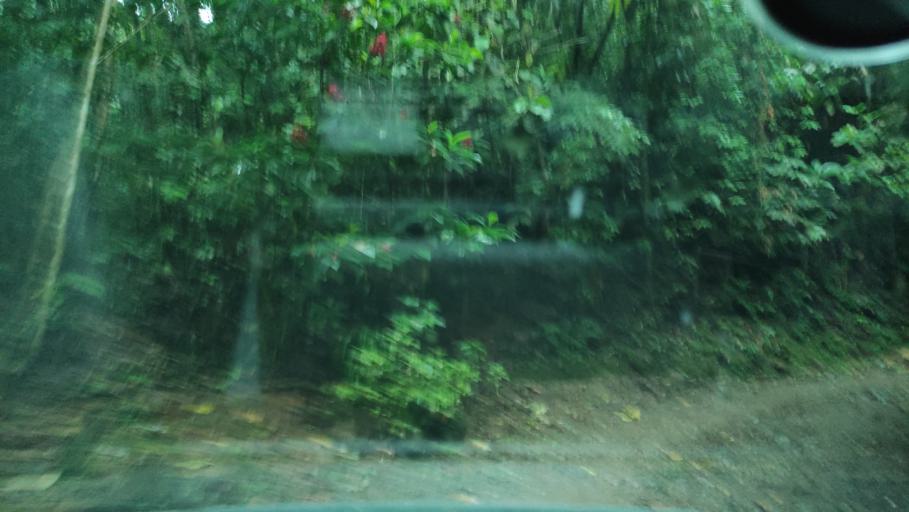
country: CO
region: Valle del Cauca
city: Jamundi
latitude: 3.3180
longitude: -76.6356
